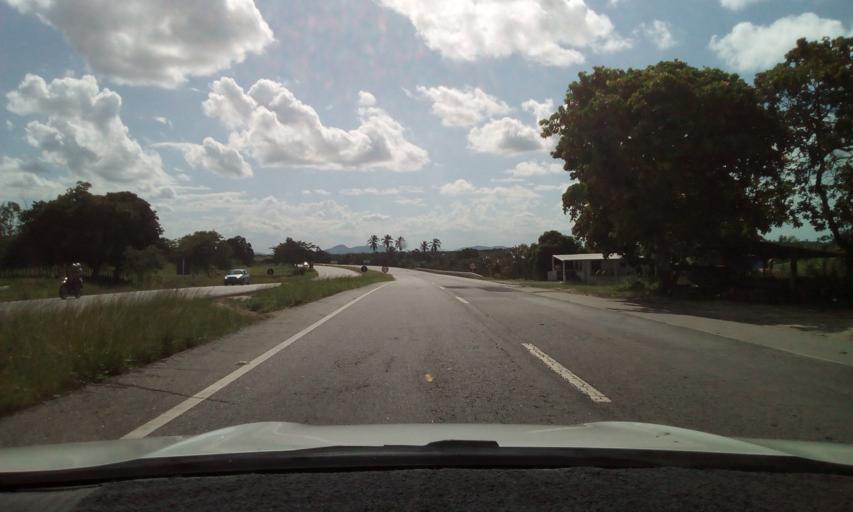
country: BR
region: Paraiba
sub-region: Pilar
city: Pilar
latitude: -7.1895
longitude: -35.2588
